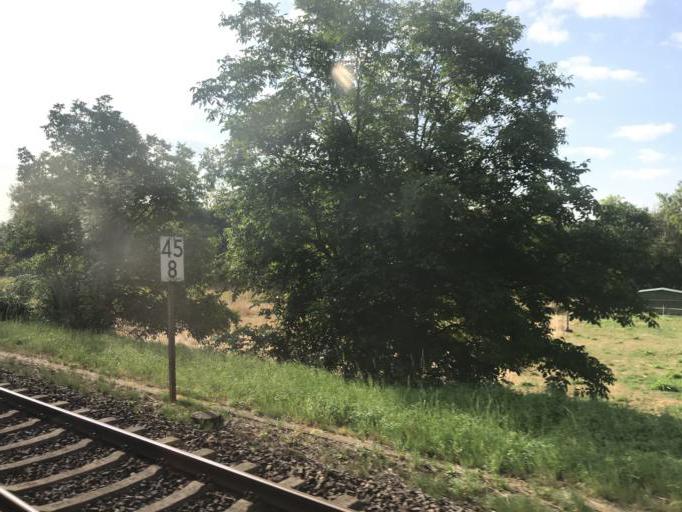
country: DE
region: Rheinland-Pfalz
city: Martinstein
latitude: 49.8013
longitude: 7.5528
